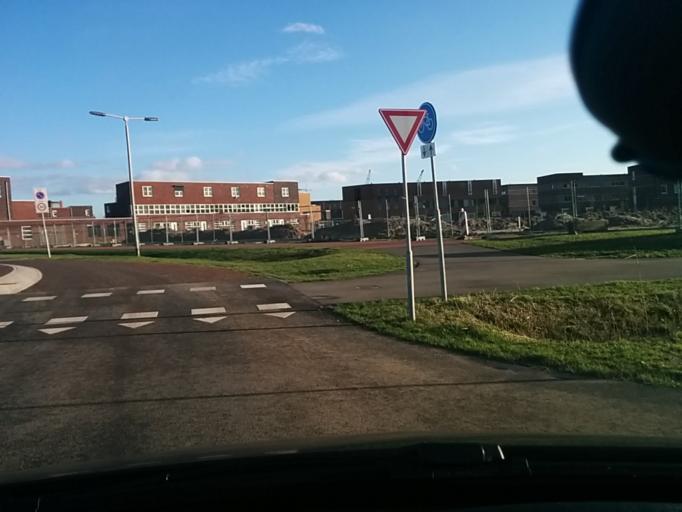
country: NL
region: Gelderland
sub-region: Gemeente Overbetuwe
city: Driel
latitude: 51.9522
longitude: 5.8457
